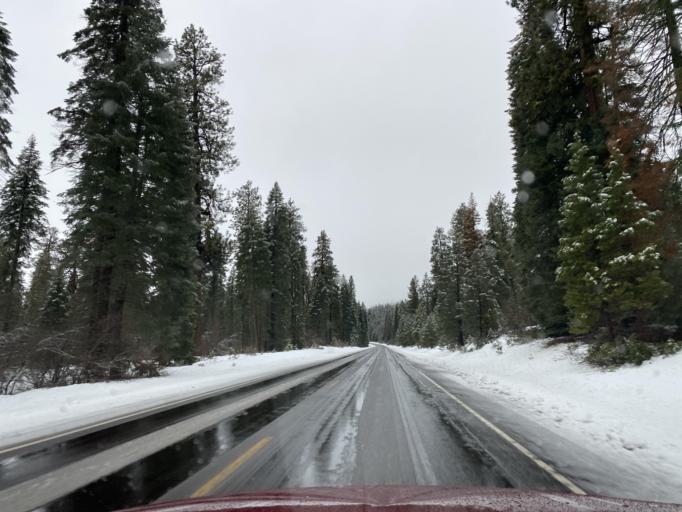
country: US
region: Oregon
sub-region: Klamath County
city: Klamath Falls
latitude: 42.5433
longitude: -122.0883
